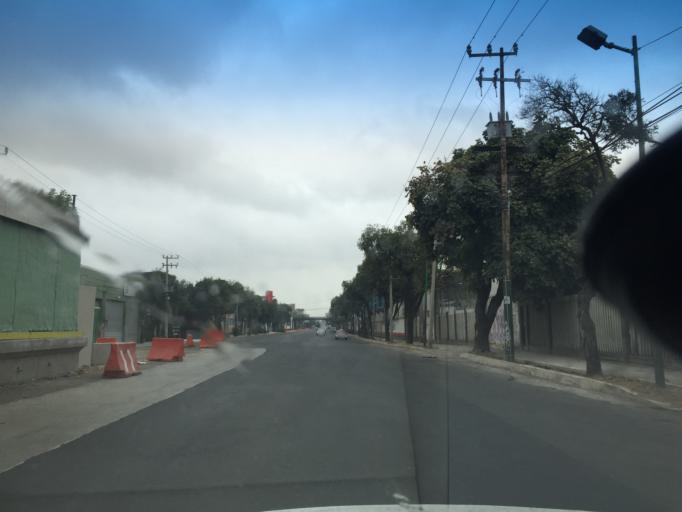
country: MX
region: Mexico City
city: Azcapotzalco
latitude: 19.4965
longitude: -99.1600
